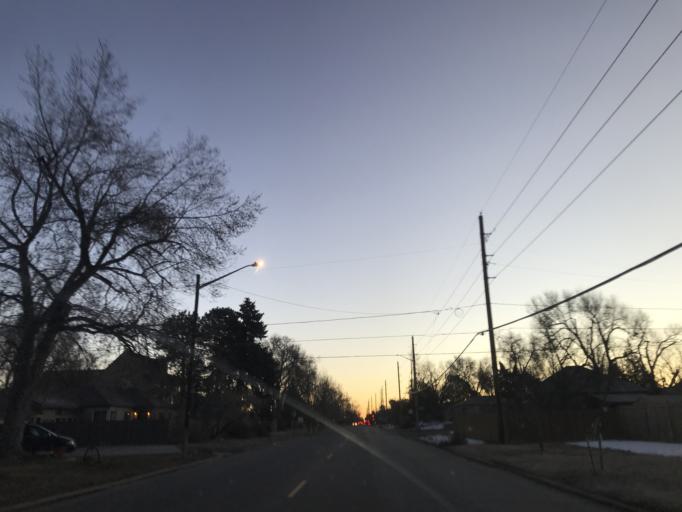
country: US
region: Colorado
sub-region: Arapahoe County
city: Glendale
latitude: 39.7438
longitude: -104.9069
